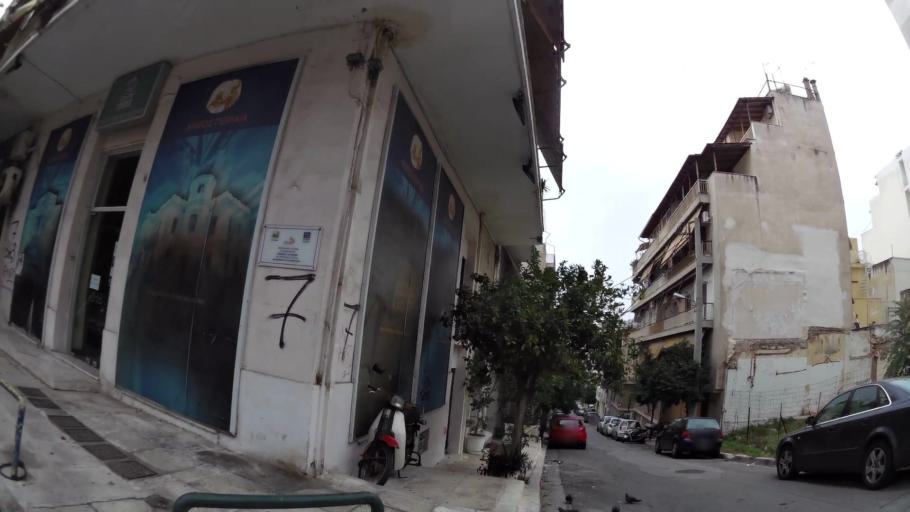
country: GR
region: Attica
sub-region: Nomos Attikis
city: Piraeus
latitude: 37.9320
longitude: 23.6404
